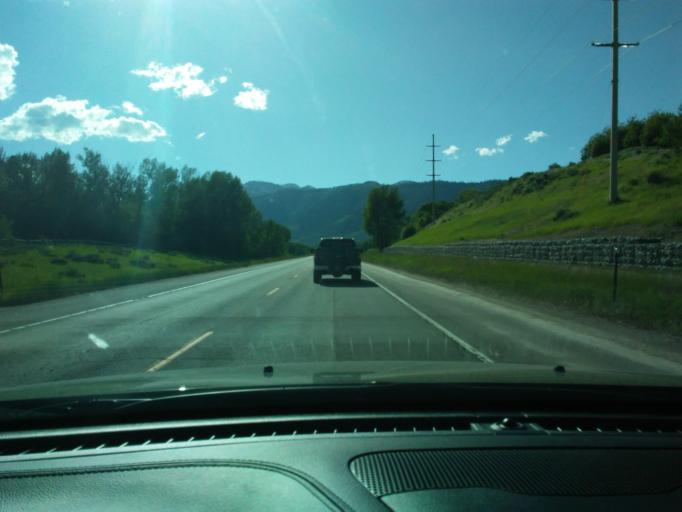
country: US
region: Wyoming
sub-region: Teton County
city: Moose Wilson Road
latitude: 43.4976
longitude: -110.8350
